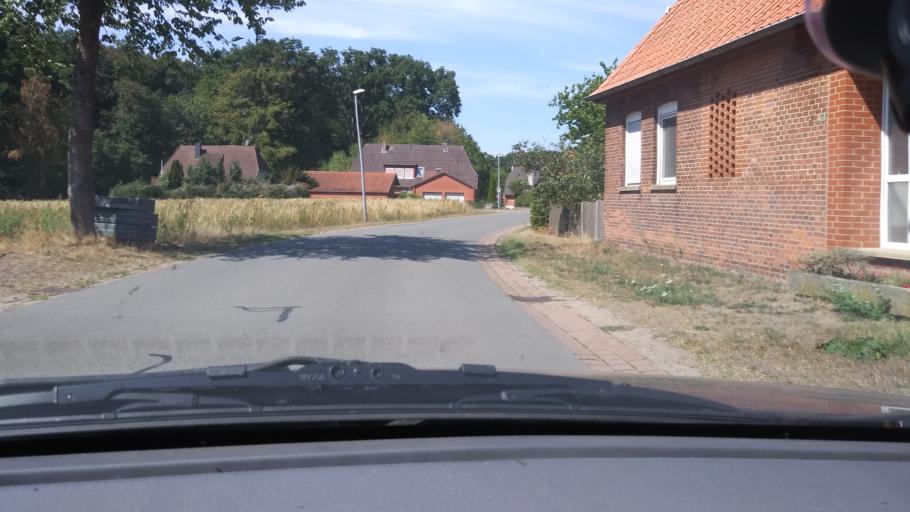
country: DE
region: Lower Saxony
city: Binnen
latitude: 52.6200
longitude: 9.1276
